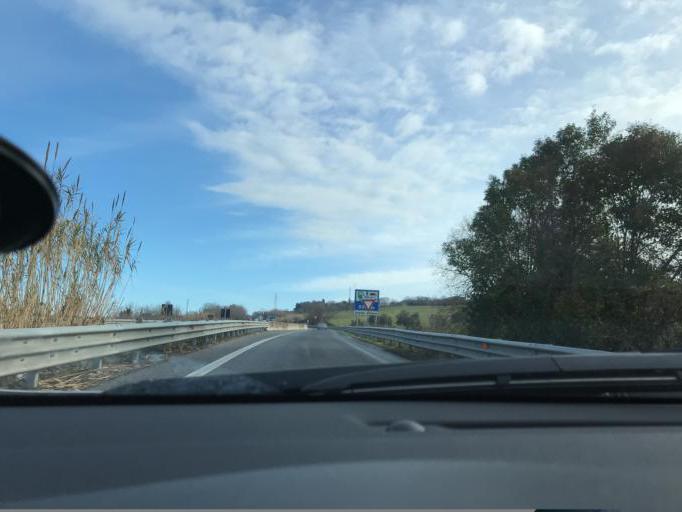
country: IT
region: The Marches
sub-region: Provincia di Ancona
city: Falconara Marittima
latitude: 43.6139
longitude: 13.3863
